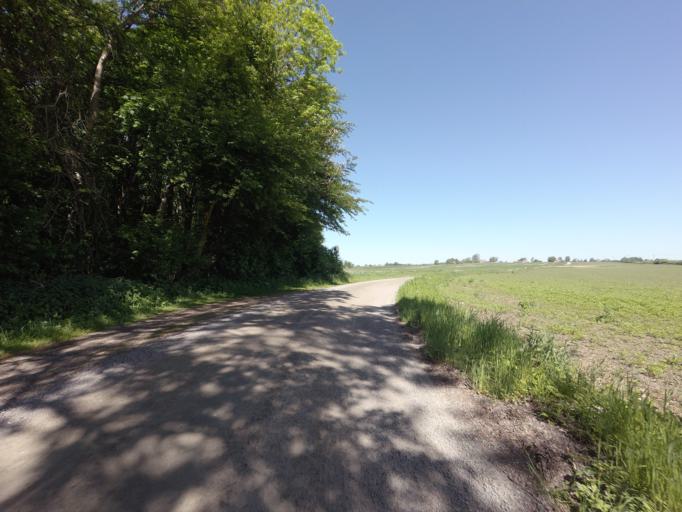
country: SE
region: Skane
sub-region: Helsingborg
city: Odakra
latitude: 56.0975
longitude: 12.7177
